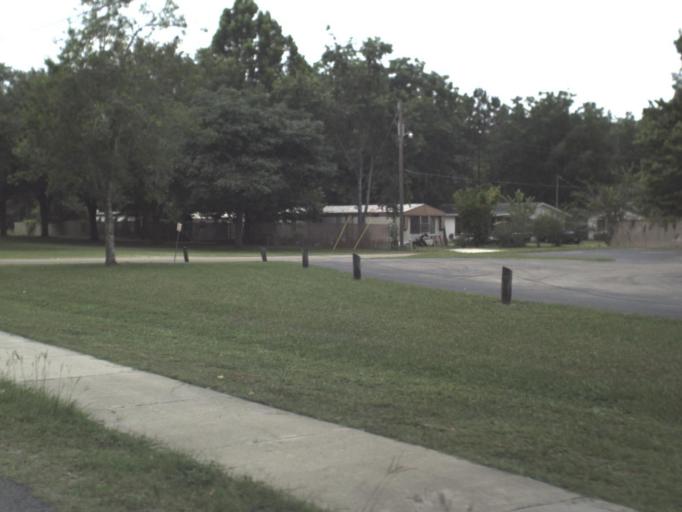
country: US
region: Florida
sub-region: Levy County
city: Chiefland
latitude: 29.4748
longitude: -82.8648
